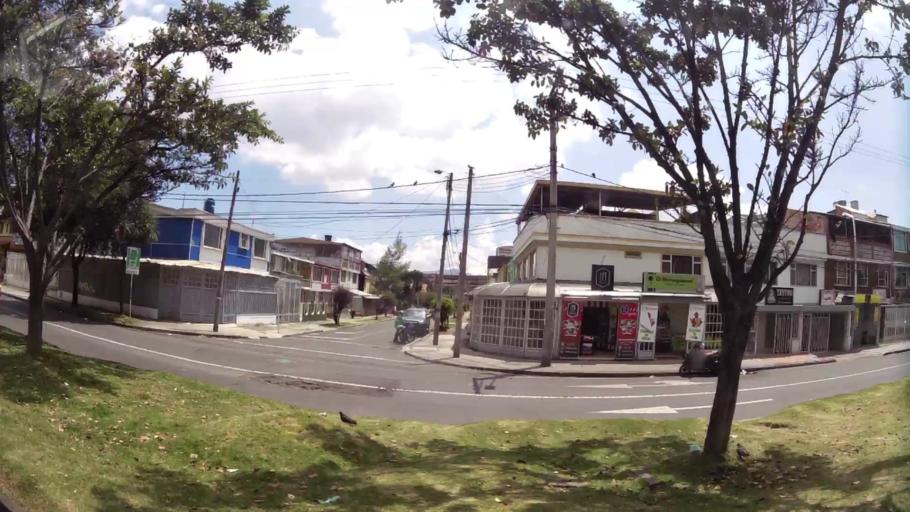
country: CO
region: Bogota D.C.
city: Bogota
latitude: 4.5844
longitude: -74.0931
